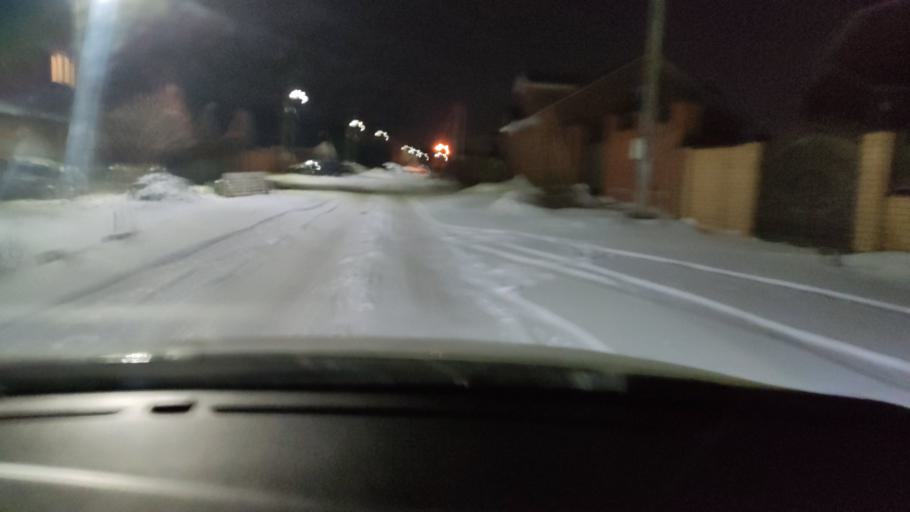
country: RU
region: Tatarstan
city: Vysokaya Gora
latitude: 55.8386
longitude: 49.2423
